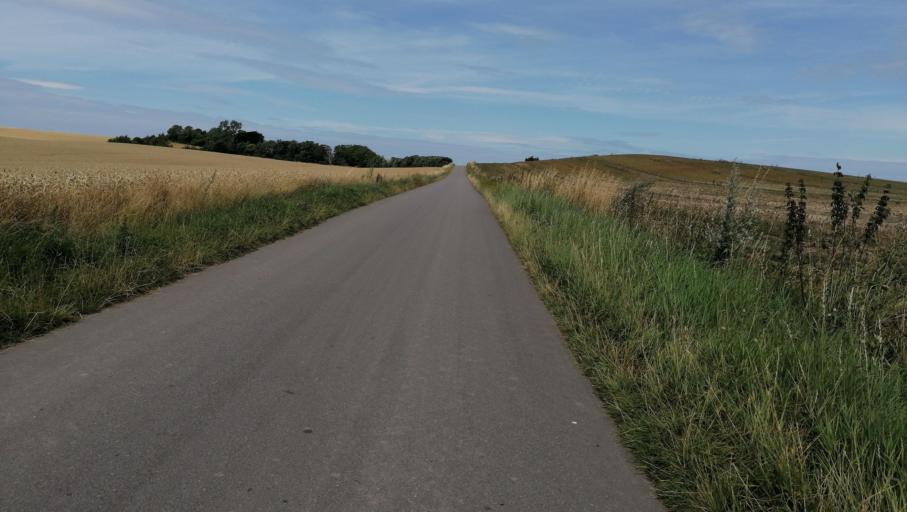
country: DK
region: Zealand
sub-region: Odsherred Kommune
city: Horve
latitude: 55.7609
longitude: 11.4542
